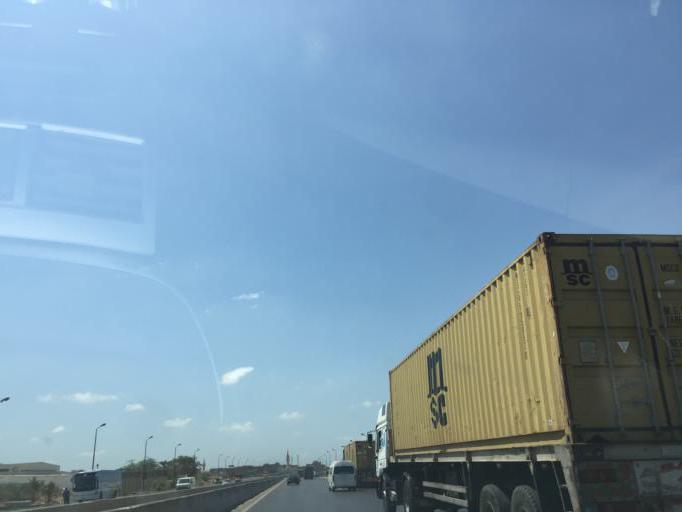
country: EG
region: Alexandria
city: Alexandria
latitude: 30.9753
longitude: 29.8206
